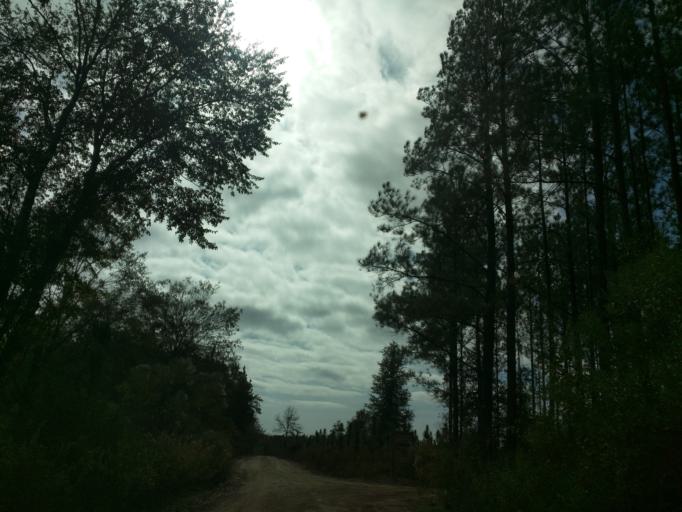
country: US
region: Florida
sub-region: Escambia County
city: Cantonment
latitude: 30.5391
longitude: -87.4361
